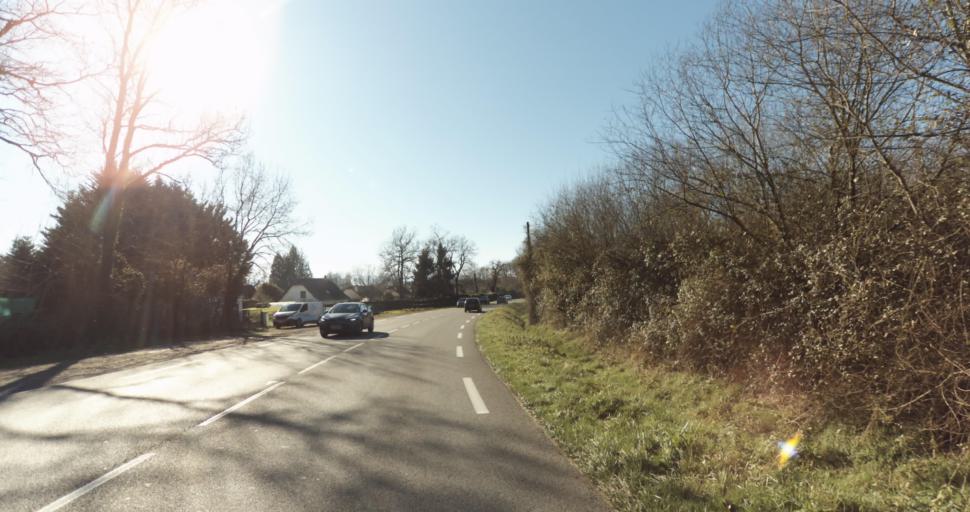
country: FR
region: Aquitaine
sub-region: Departement des Pyrenees-Atlantiques
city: Morlaas
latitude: 43.3306
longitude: -0.2831
